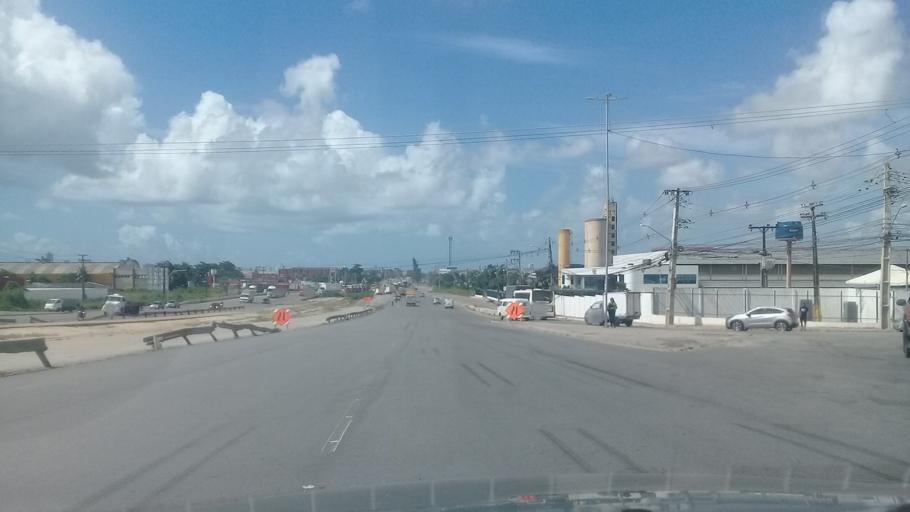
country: BR
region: Pernambuco
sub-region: Jaboatao Dos Guararapes
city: Jaboatao
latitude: -8.1541
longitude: -34.9423
